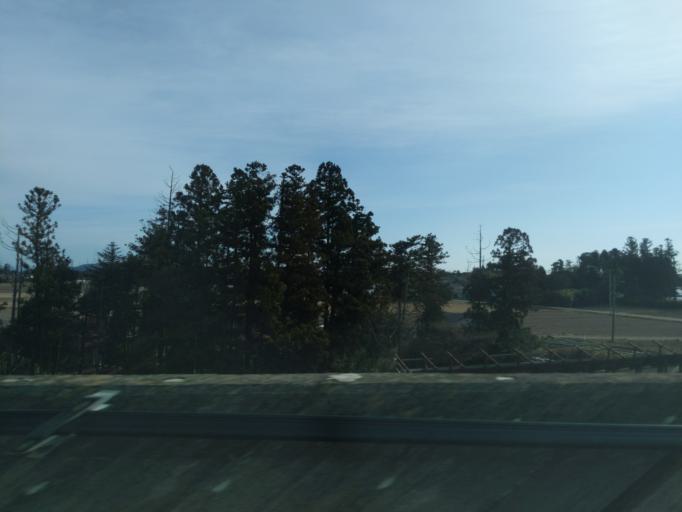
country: JP
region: Miyagi
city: Furukawa
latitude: 38.6046
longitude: 140.9857
